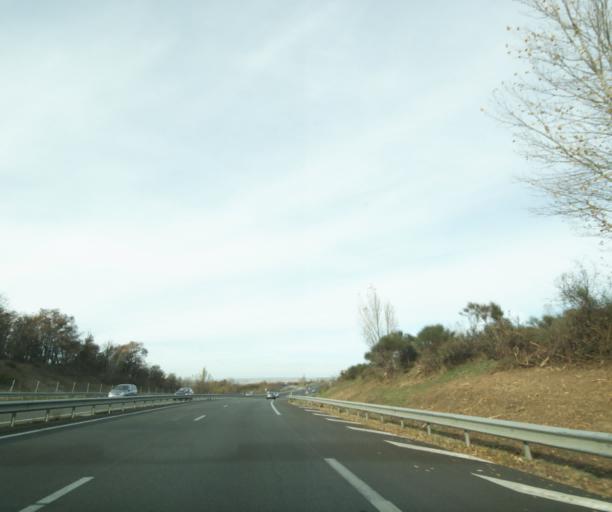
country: FR
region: Midi-Pyrenees
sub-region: Departement du Gers
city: Pujaudran
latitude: 43.5848
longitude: 1.1274
